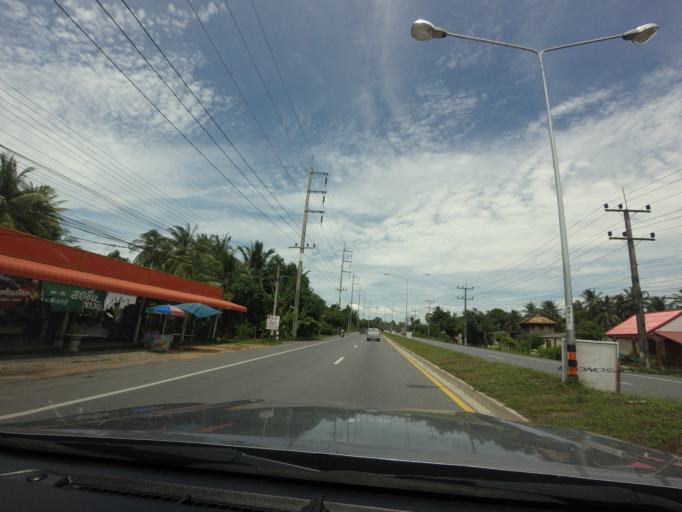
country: TH
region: Songkhla
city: Krasae Sin
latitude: 7.5979
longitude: 100.4022
